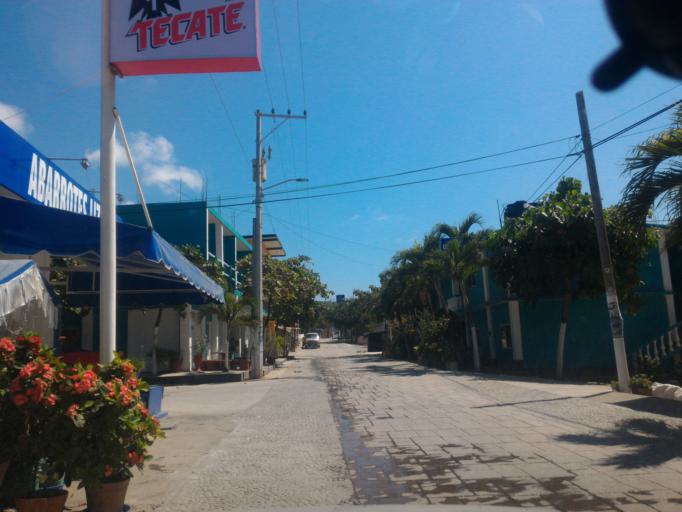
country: MX
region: Michoacan
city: Coahuayana Viejo
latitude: 18.5808
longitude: -103.6701
